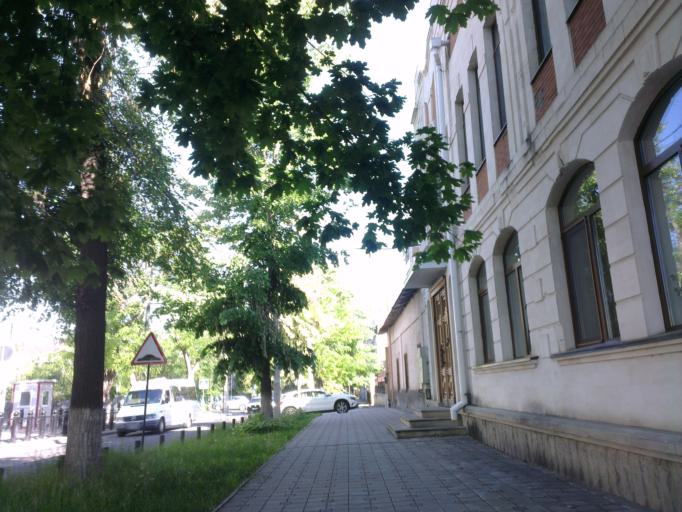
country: MD
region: Chisinau
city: Chisinau
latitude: 47.0219
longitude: 28.8194
